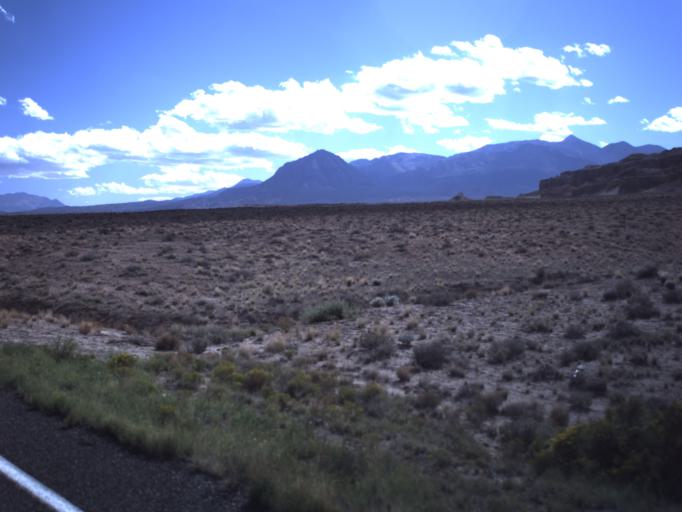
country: US
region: Utah
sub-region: Emery County
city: Ferron
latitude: 38.2778
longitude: -110.6615
